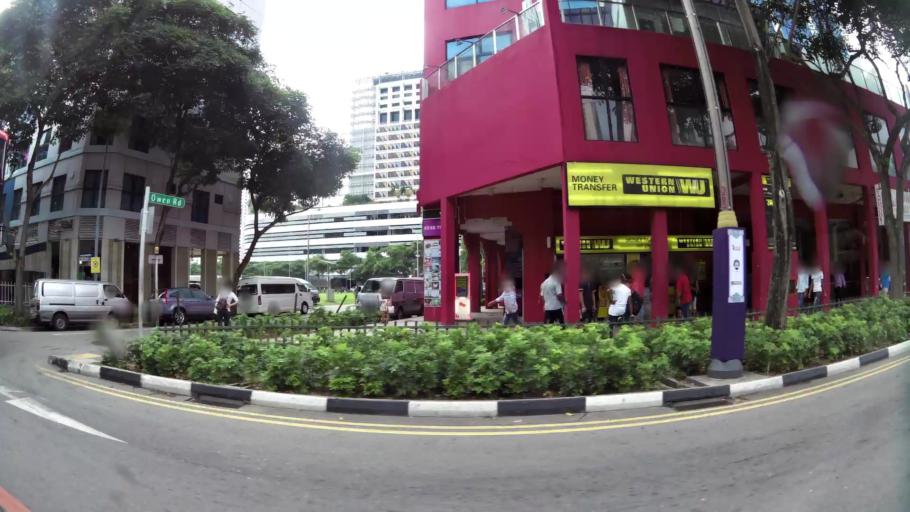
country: SG
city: Singapore
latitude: 1.3116
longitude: 103.8549
